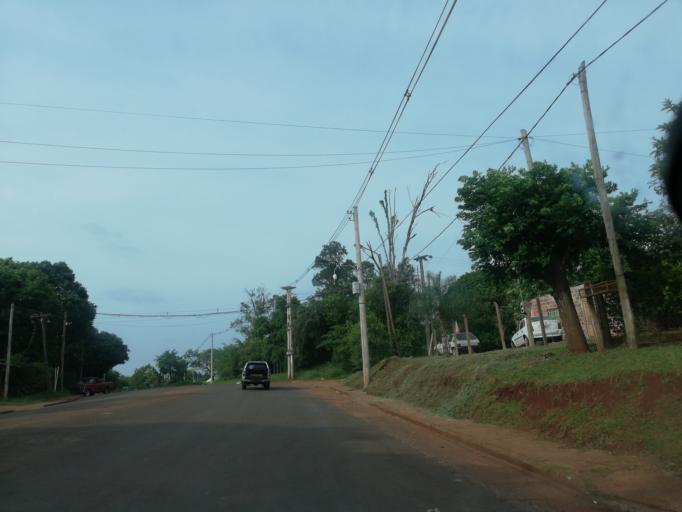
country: AR
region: Misiones
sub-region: Departamento de Capital
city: Posadas
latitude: -27.4175
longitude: -55.9210
